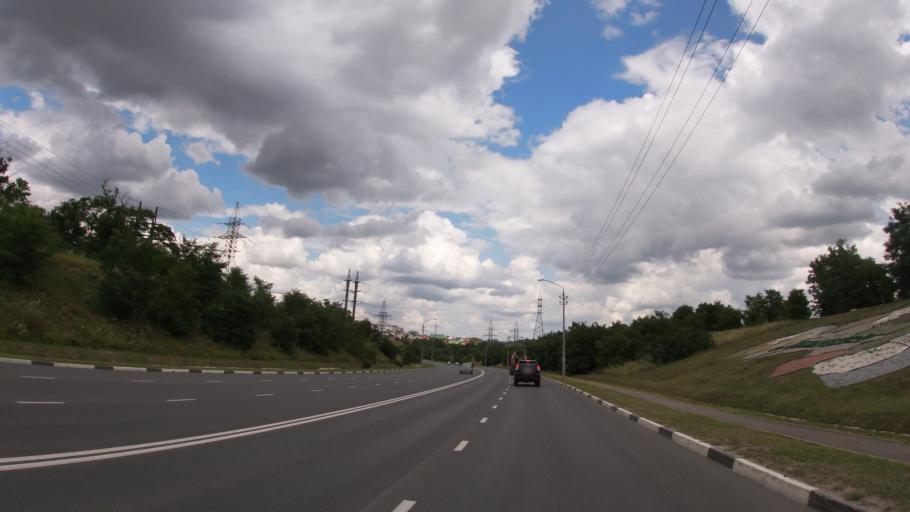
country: RU
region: Belgorod
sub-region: Belgorodskiy Rayon
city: Belgorod
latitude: 50.5561
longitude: 36.5847
